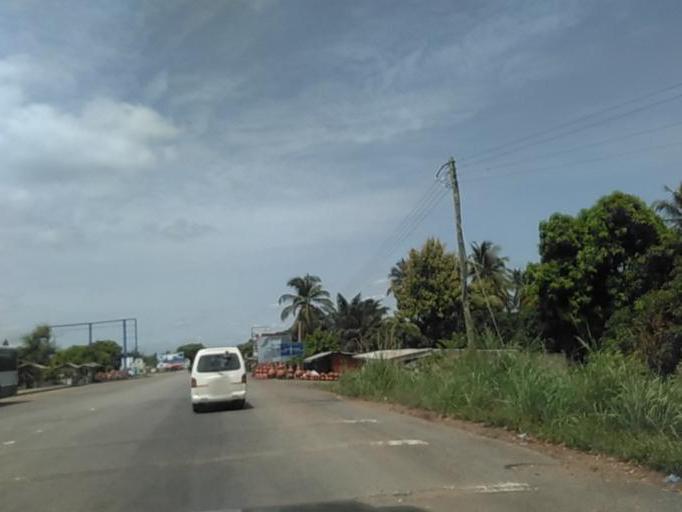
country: GH
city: Akropong
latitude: 6.0953
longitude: 0.0444
